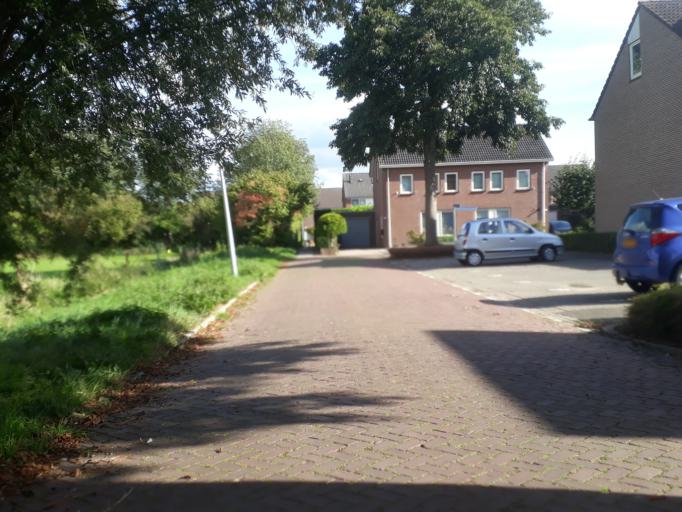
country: NL
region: Gelderland
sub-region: Gemeente Zevenaar
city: Zevenaar
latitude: 51.9312
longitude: 6.0503
